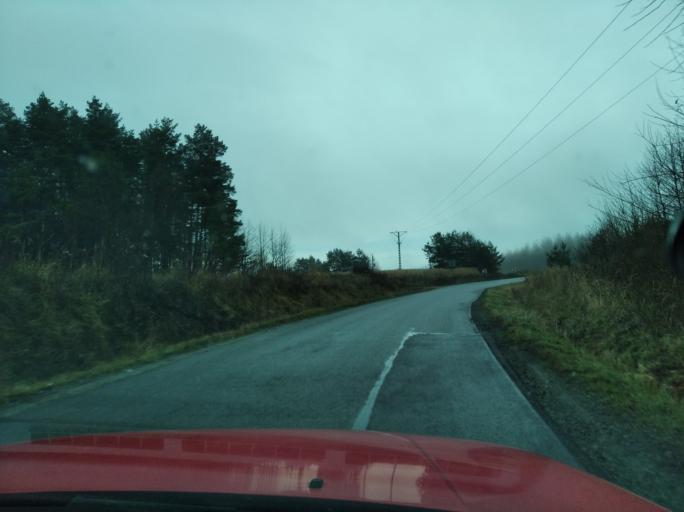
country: PL
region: Subcarpathian Voivodeship
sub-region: Powiat jaroslawski
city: Jodlowka
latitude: 49.8796
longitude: 22.4311
